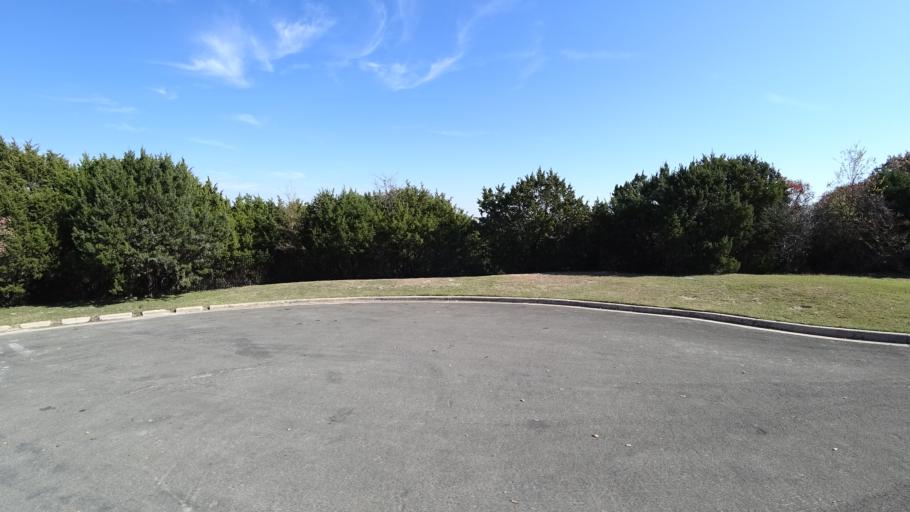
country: US
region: Texas
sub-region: Travis County
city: West Lake Hills
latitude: 30.3689
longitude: -97.7810
